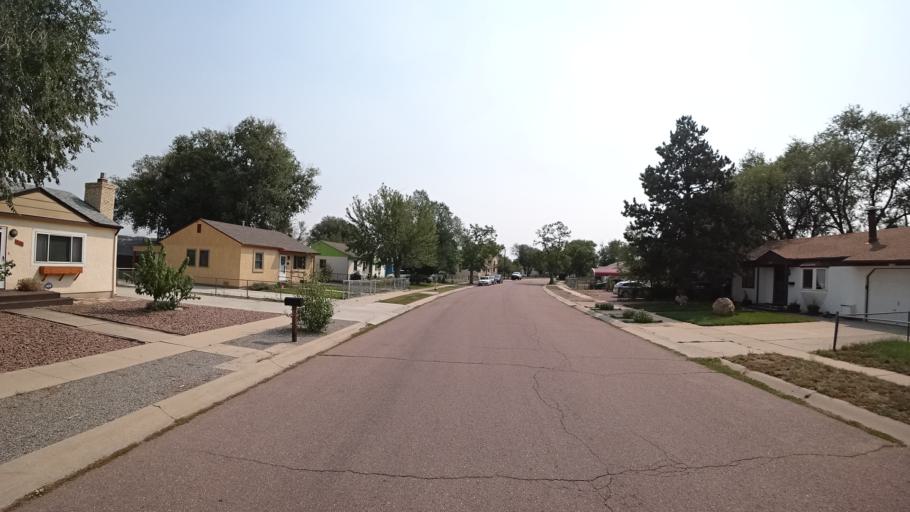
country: US
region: Colorado
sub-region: El Paso County
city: Colorado Springs
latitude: 38.8100
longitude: -104.8165
